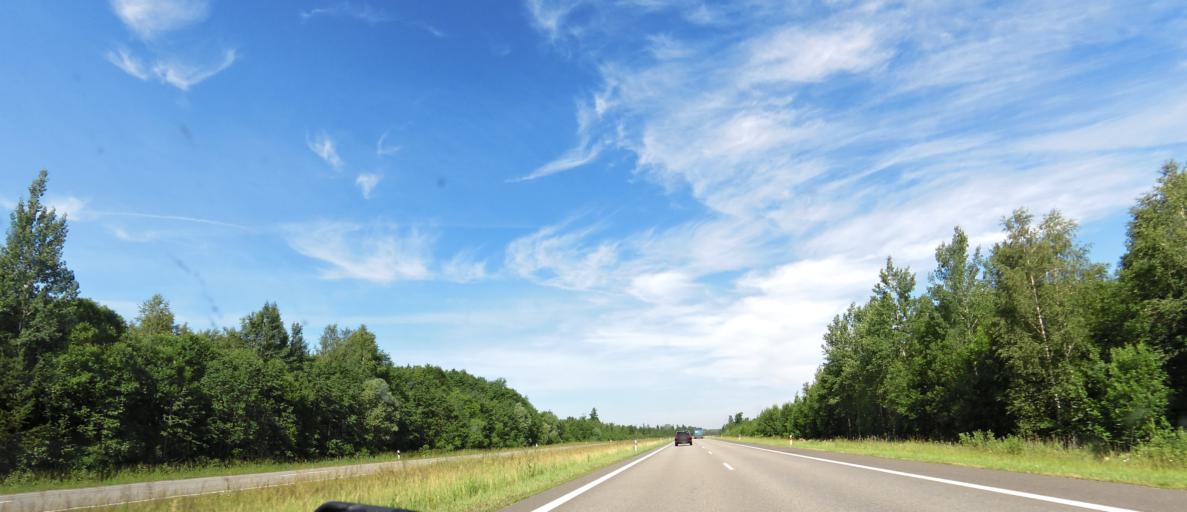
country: LT
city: Ramygala
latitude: 55.5292
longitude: 24.5611
